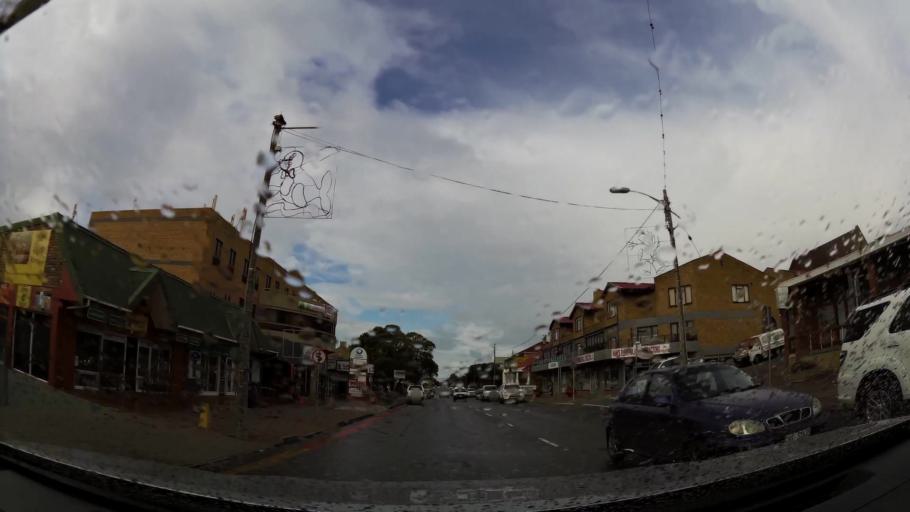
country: ZA
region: Western Cape
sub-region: Eden District Municipality
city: Mossel Bay
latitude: -34.1827
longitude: 22.1469
